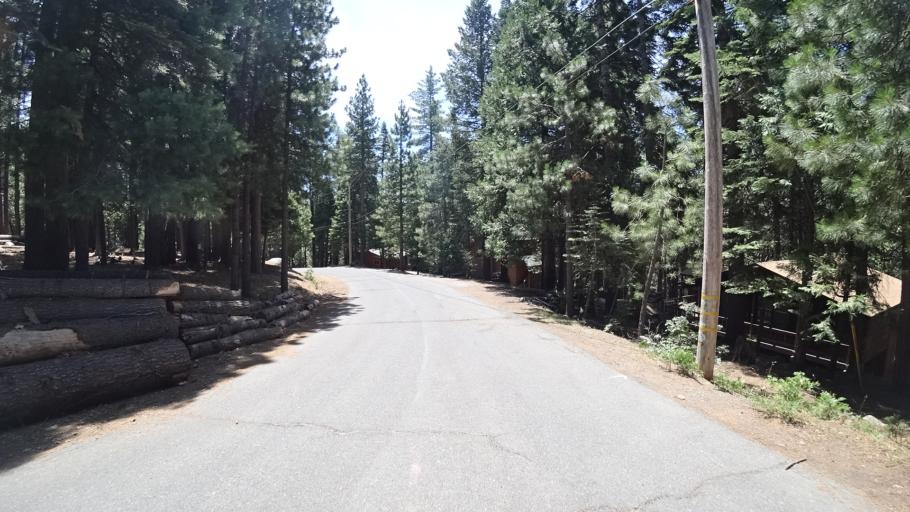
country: US
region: California
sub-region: Calaveras County
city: Arnold
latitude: 38.3202
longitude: -120.2548
